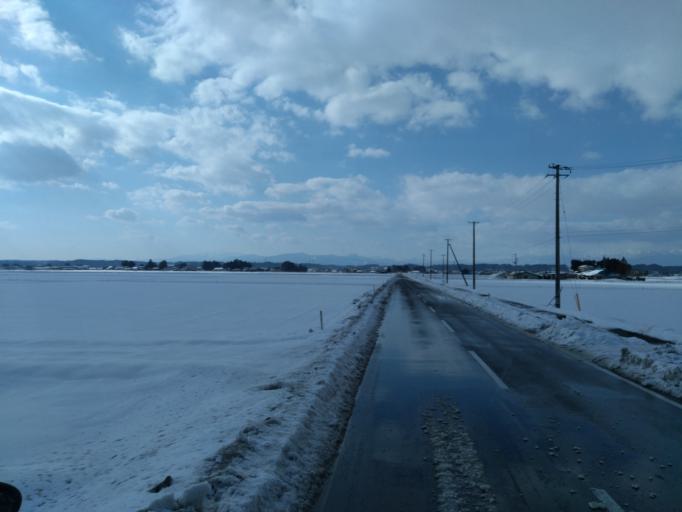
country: JP
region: Iwate
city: Mizusawa
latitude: 39.0986
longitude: 141.1677
